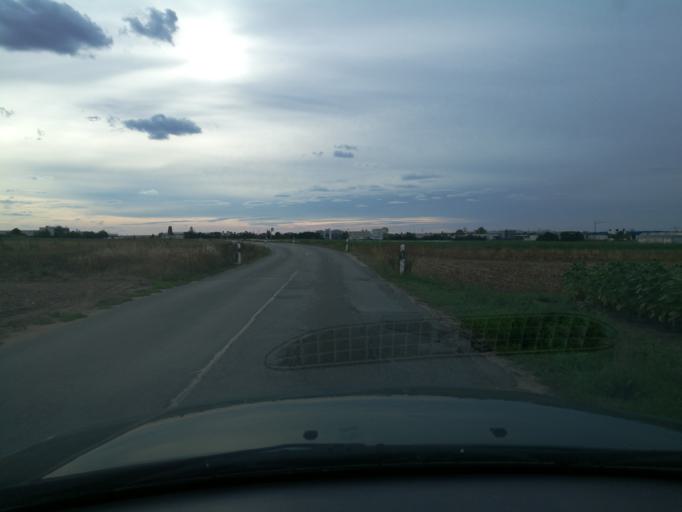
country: DE
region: Bavaria
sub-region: Regierungsbezirk Mittelfranken
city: Furth
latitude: 49.5154
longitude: 11.0171
